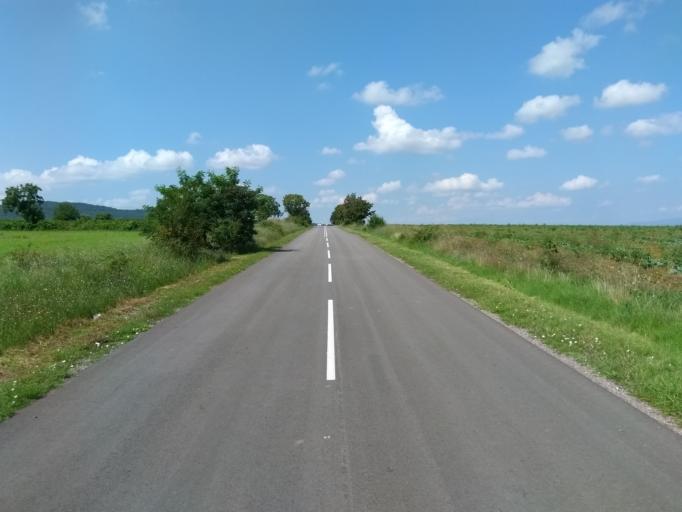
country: BG
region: Sliven
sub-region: Obshtina Nova Zagora
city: Nova Zagora
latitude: 42.4568
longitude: 26.1324
